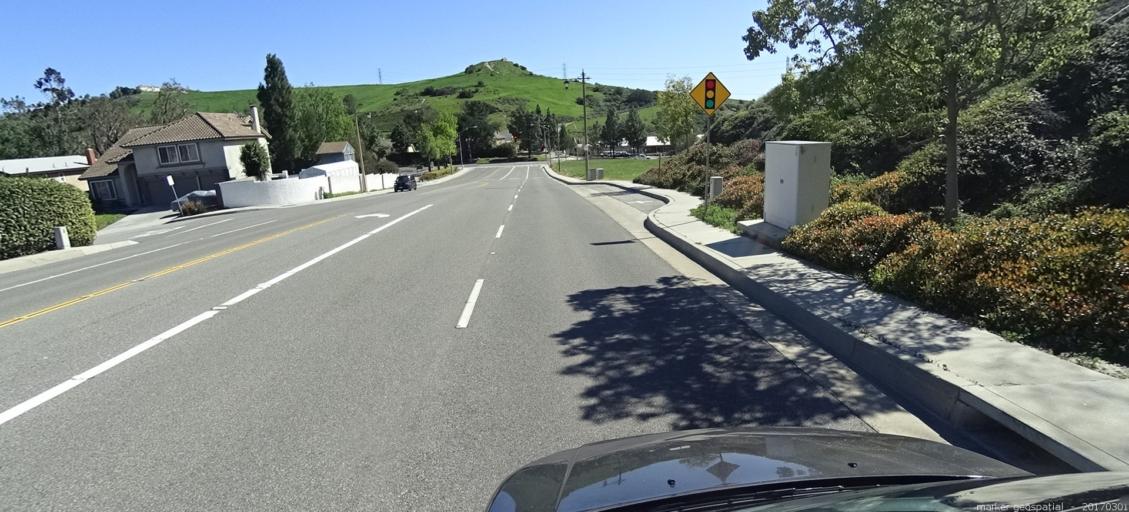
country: US
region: California
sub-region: Orange County
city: Villa Park
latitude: 33.8321
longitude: -117.7616
